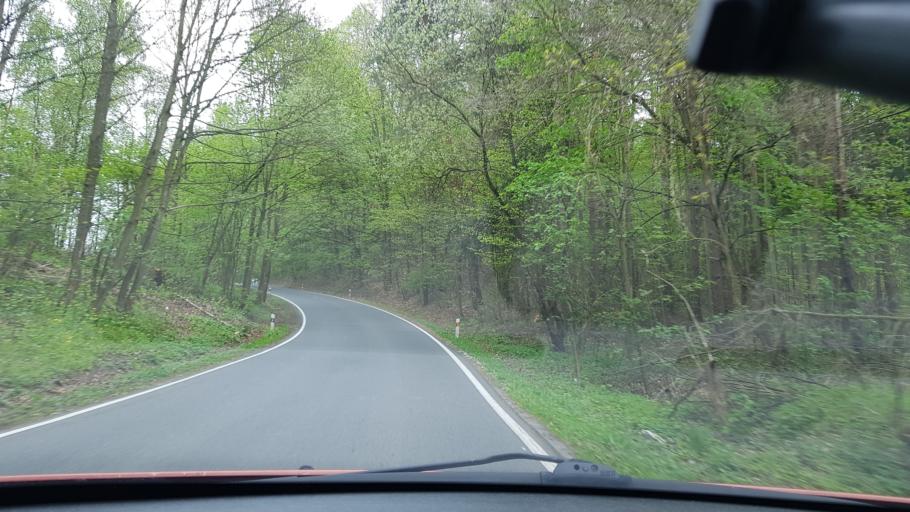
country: CZ
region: Olomoucky
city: Vidnava
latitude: 50.3665
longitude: 17.1950
